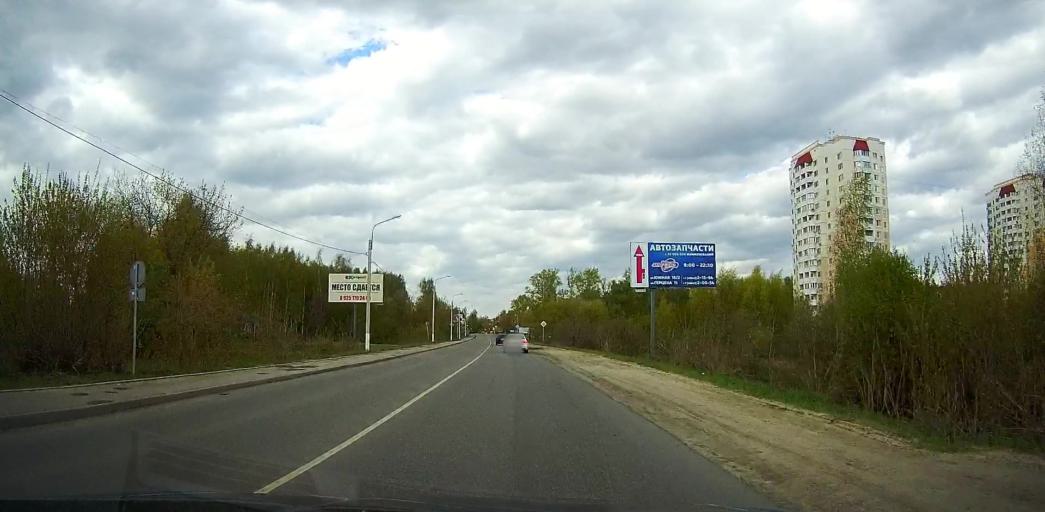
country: RU
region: Moskovskaya
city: Pavlovskiy Posad
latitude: 55.7637
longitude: 38.6567
